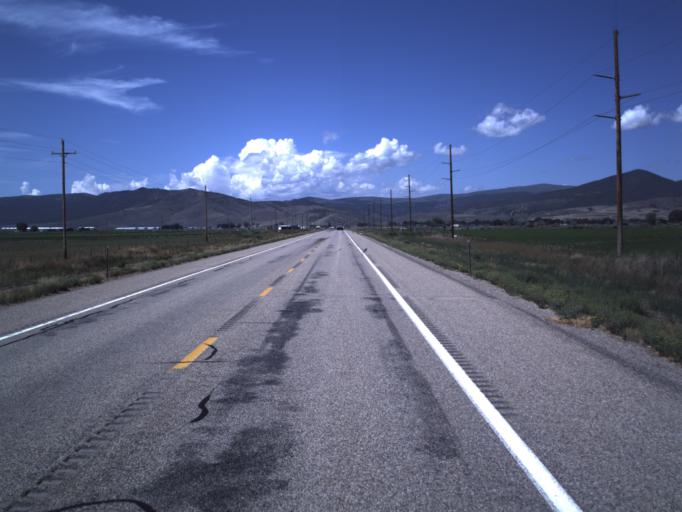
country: US
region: Utah
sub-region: Piute County
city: Junction
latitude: 38.1836
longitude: -112.2453
